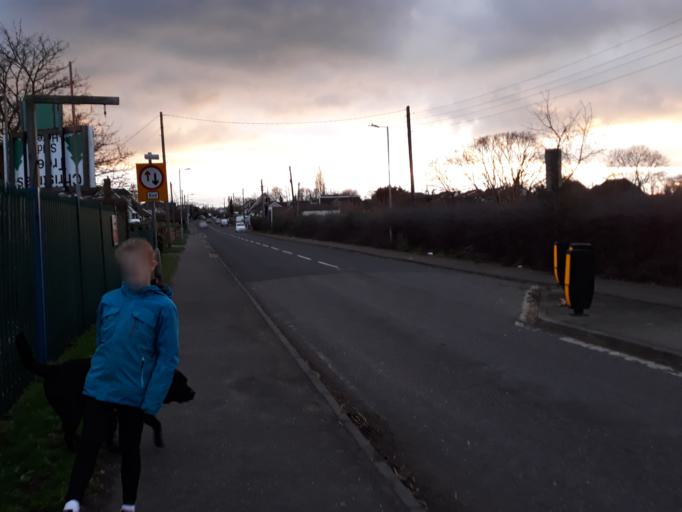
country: GB
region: England
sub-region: Essex
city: Pitsea
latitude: 51.5738
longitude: 0.5327
